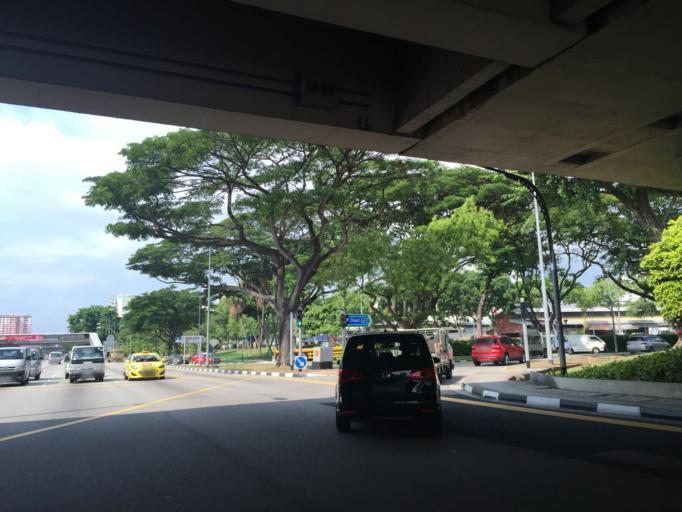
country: SG
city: Singapore
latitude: 1.3229
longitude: 103.8909
